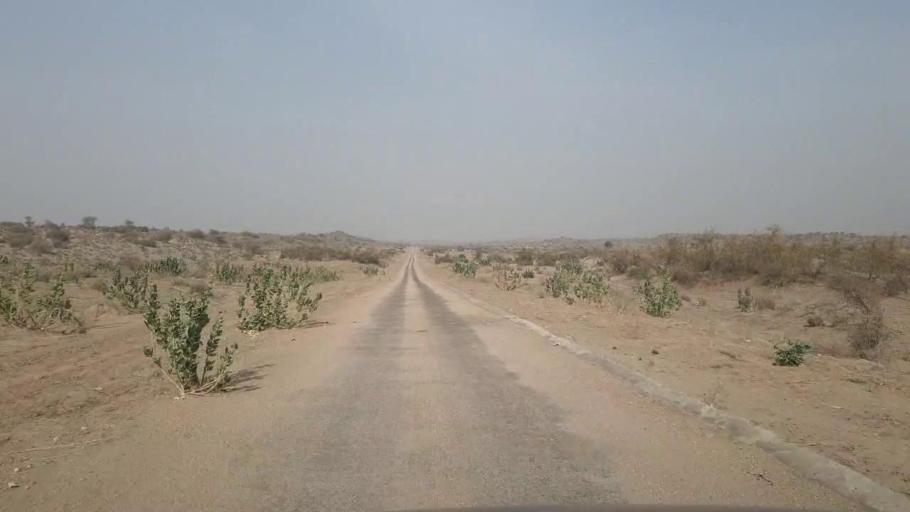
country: PK
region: Sindh
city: Chor
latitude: 25.6178
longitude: 69.9314
